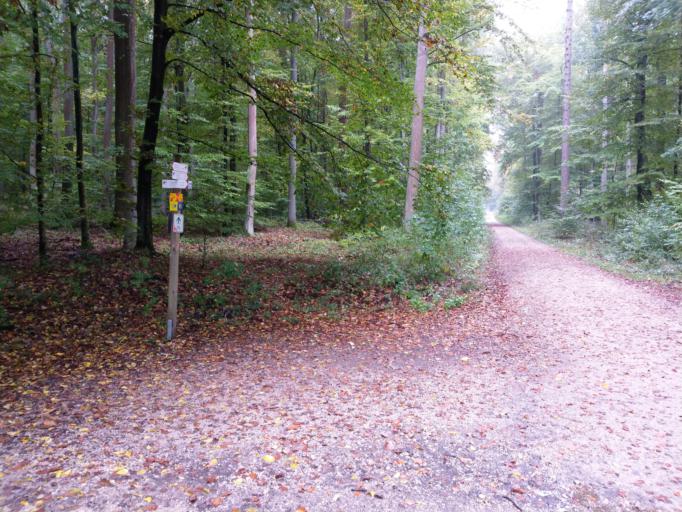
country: DE
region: Bavaria
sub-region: Lower Bavaria
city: Ihrlerstein
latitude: 48.9034
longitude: 11.8331
